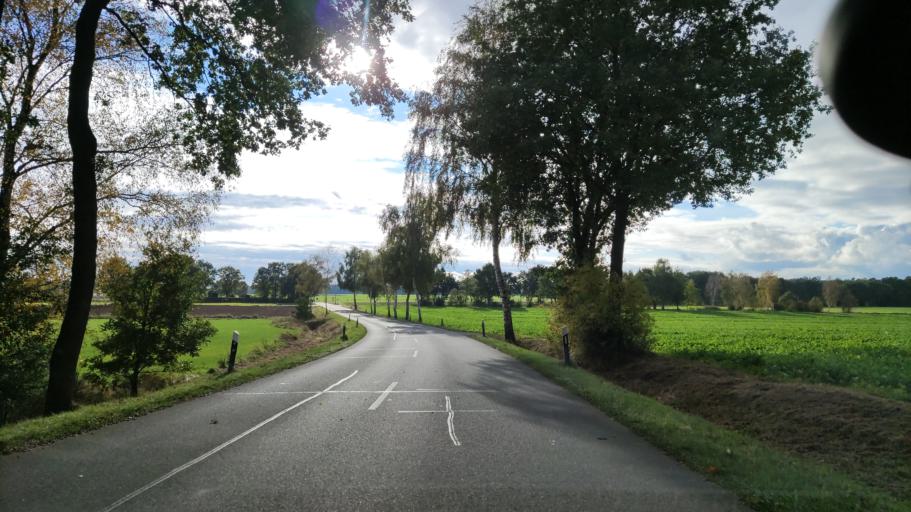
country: DE
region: Lower Saxony
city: Romstedt
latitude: 53.0849
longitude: 10.6396
